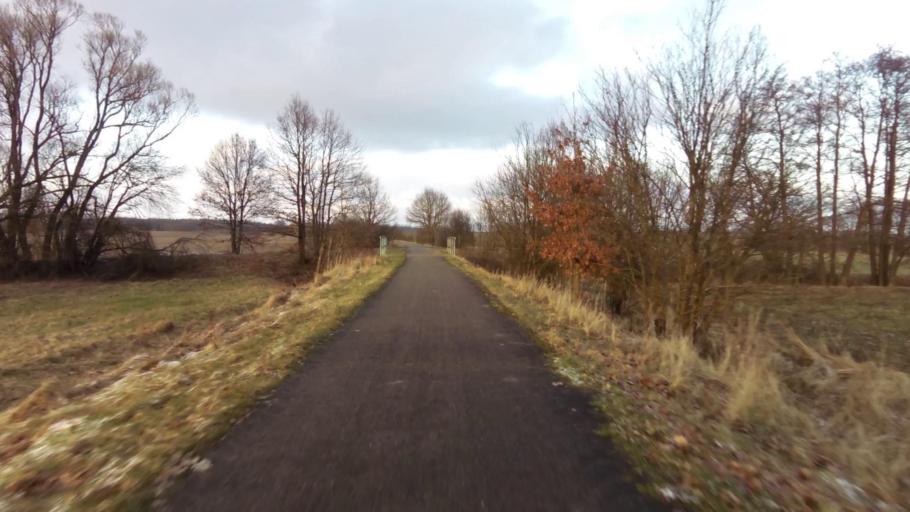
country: PL
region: West Pomeranian Voivodeship
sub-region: Powiat drawski
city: Zlocieniec
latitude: 53.6212
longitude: 16.0564
